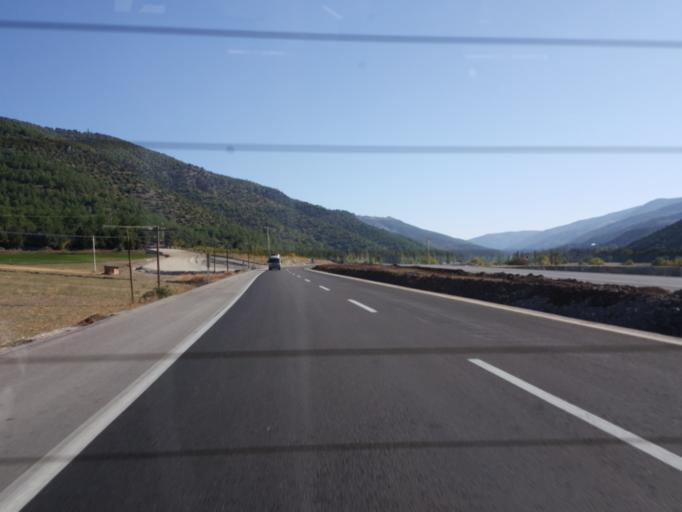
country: TR
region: Tokat
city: Turhal
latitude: 40.4696
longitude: 36.1266
